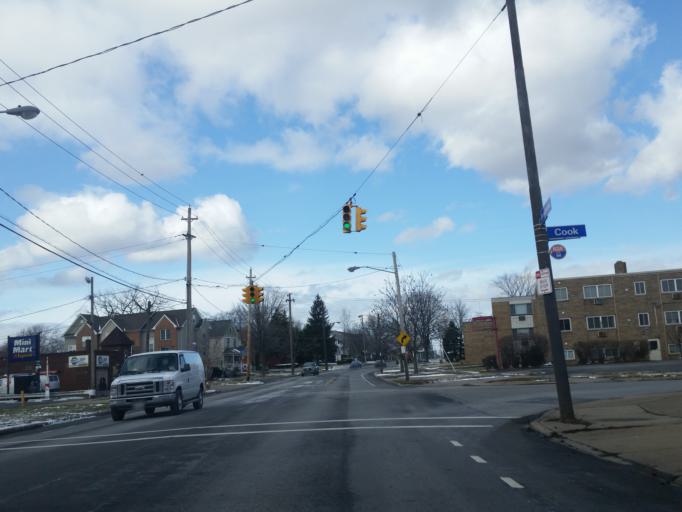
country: US
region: Ohio
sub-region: Cuyahoga County
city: Brooklyn Heights
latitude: 41.4235
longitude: -81.6965
